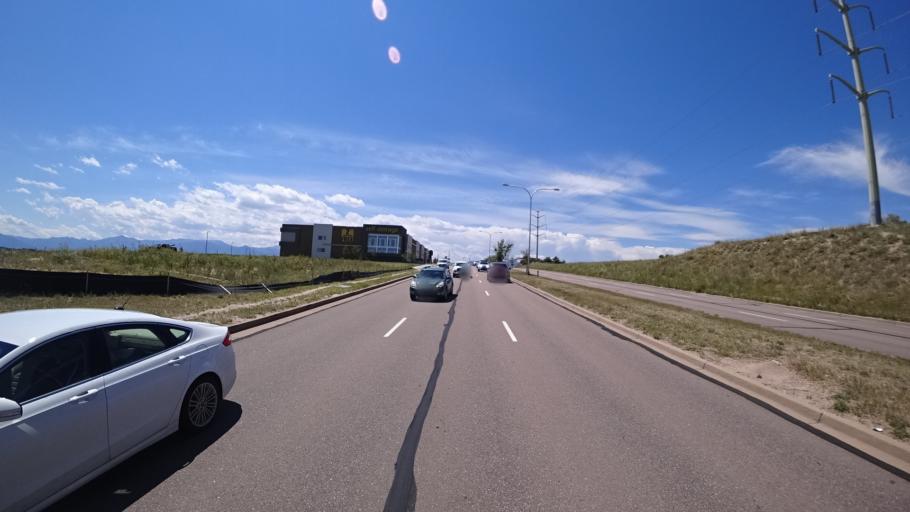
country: US
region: Colorado
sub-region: El Paso County
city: Black Forest
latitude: 38.9401
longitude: -104.7456
